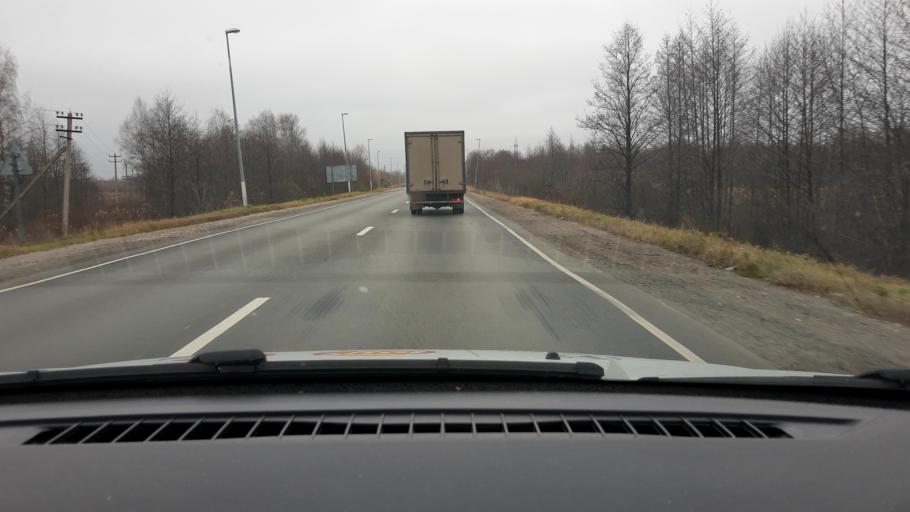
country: RU
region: Nizjnij Novgorod
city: Gorodets
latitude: 56.6106
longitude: 43.4427
